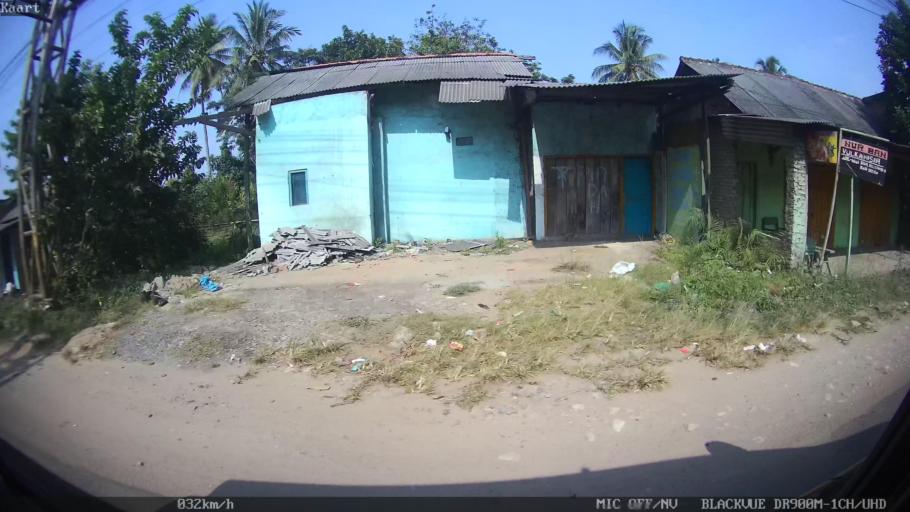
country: ID
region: Lampung
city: Natar
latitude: -5.2387
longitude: 105.1727
